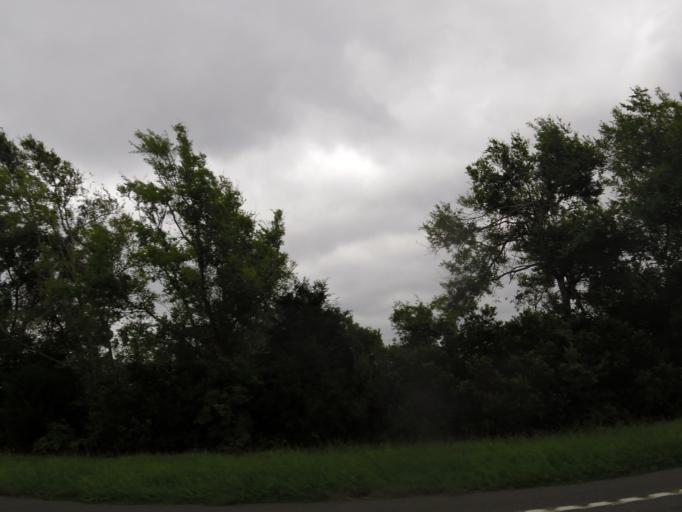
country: US
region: Georgia
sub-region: Glynn County
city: Brunswick
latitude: 31.0634
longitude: -81.4530
